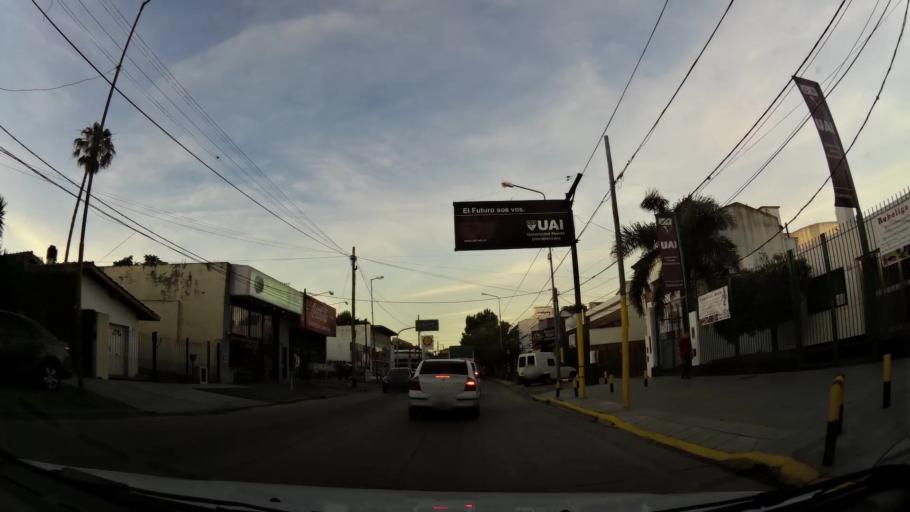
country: AR
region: Buenos Aires
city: Ituzaingo
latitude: -34.6493
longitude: -58.6582
